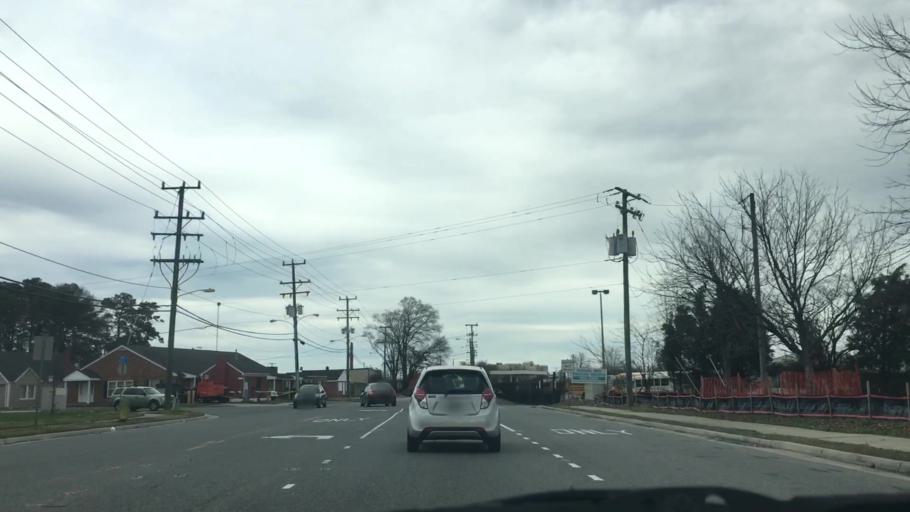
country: US
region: Virginia
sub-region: City of Norfolk
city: Norfolk
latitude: 36.8574
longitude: -76.2186
